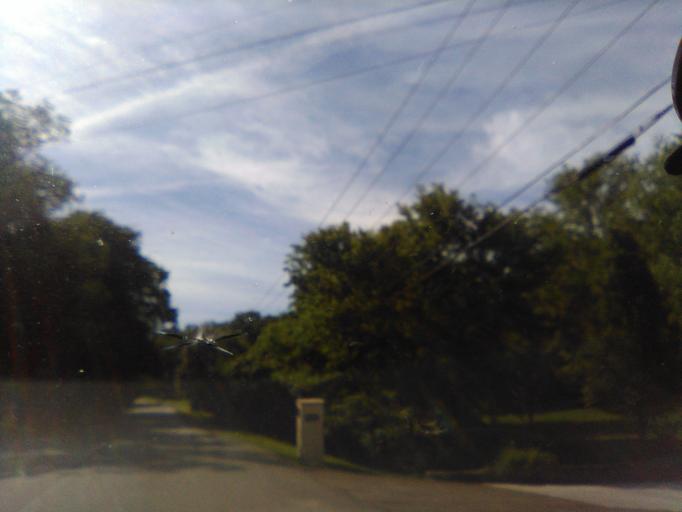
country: US
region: Tennessee
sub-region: Davidson County
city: Belle Meade
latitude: 36.1130
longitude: -86.9013
